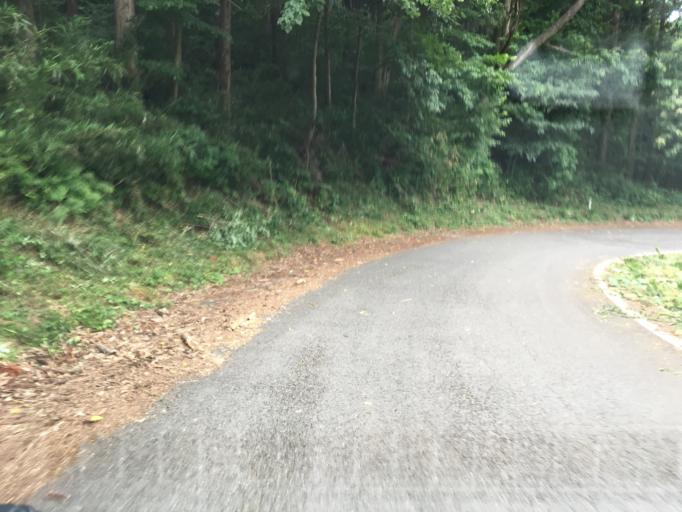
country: JP
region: Fukushima
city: Nihommatsu
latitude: 37.6345
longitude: 140.5259
